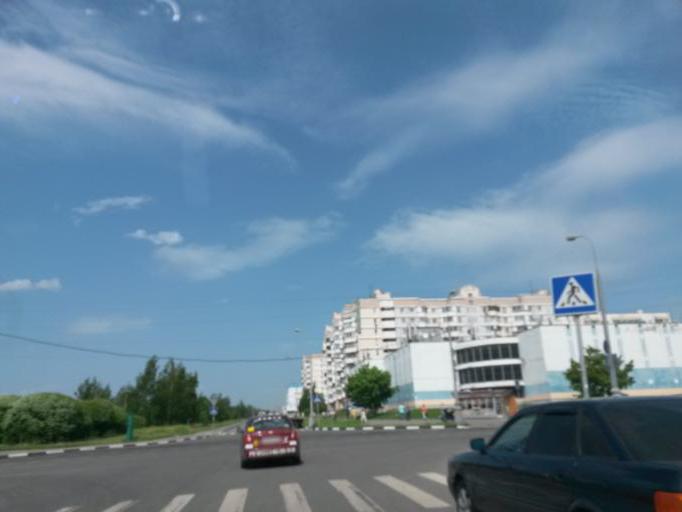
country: RU
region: Moskovskaya
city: Kommunarka
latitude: 55.5416
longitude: 37.5154
